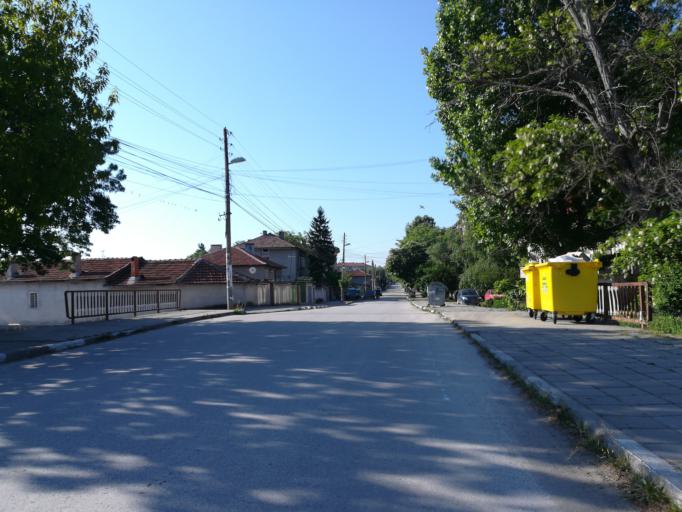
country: BG
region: Stara Zagora
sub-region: Obshtina Chirpan
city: Chirpan
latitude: 42.1056
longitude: 25.2246
